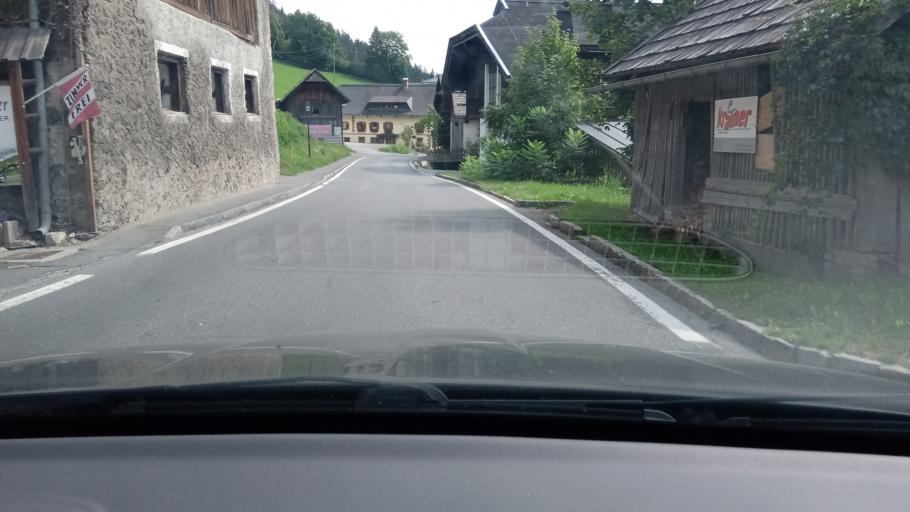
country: AT
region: Carinthia
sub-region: Politischer Bezirk Spittal an der Drau
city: Steinfeld
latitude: 46.7233
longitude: 13.2730
